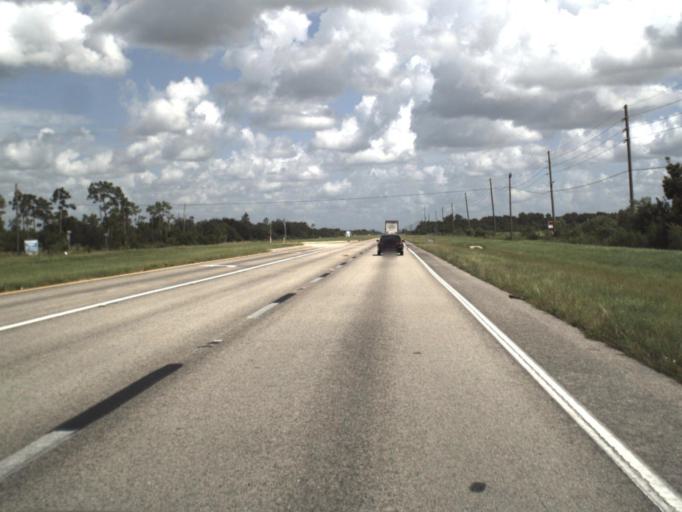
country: US
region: Florida
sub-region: Charlotte County
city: Harbour Heights
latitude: 27.0161
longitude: -81.9585
